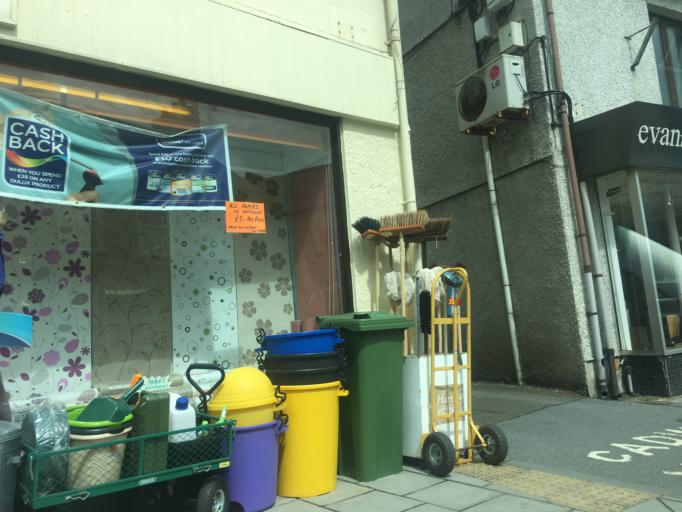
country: GB
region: Wales
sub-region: County of Ceredigion
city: Lampeter
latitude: 52.1127
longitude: -4.0779
